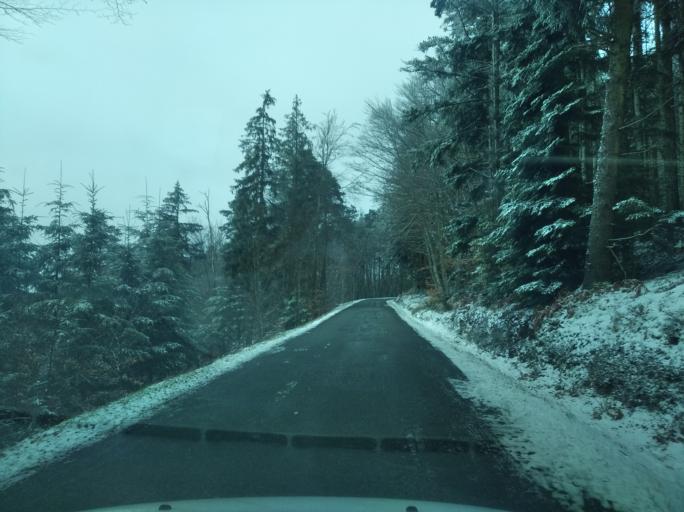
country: FR
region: Rhone-Alpes
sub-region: Departement de la Loire
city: La Pacaudiere
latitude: 46.1252
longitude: 3.7955
